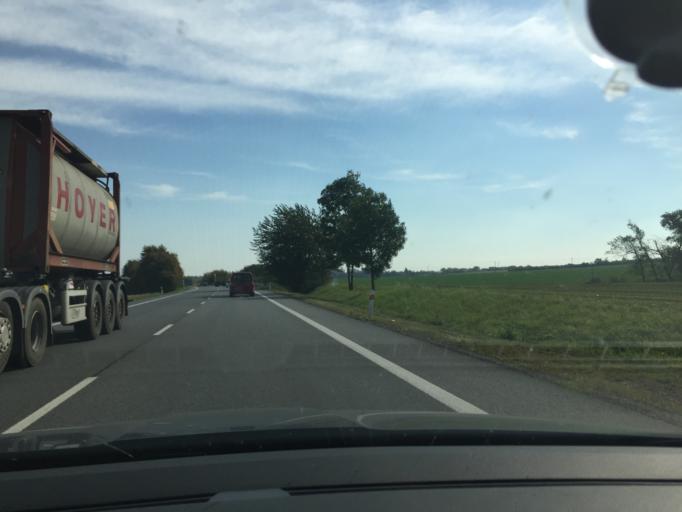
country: CZ
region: Central Bohemia
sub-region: Okres Kolin
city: Kolin
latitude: 50.0345
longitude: 15.1550
